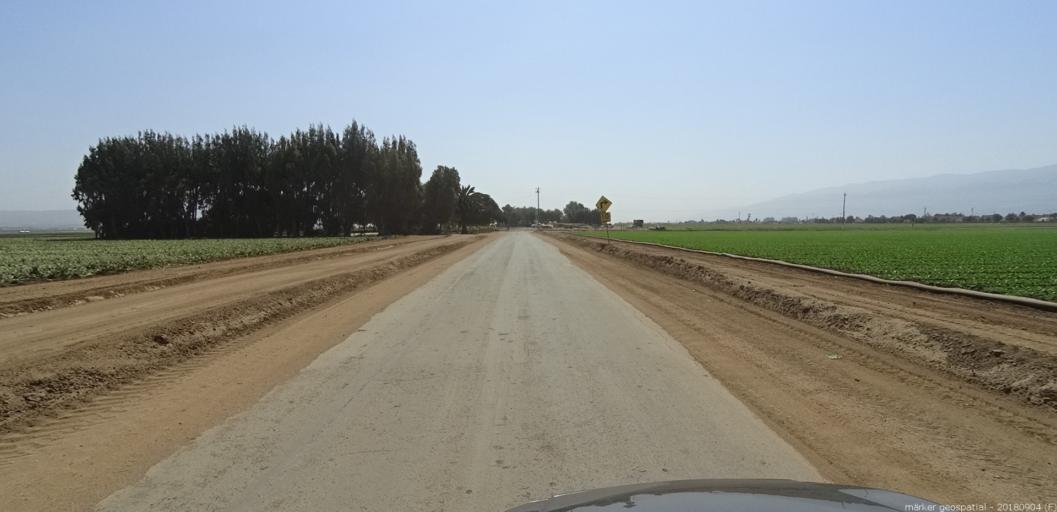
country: US
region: California
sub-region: Monterey County
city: Gonzales
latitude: 36.5291
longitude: -121.4438
